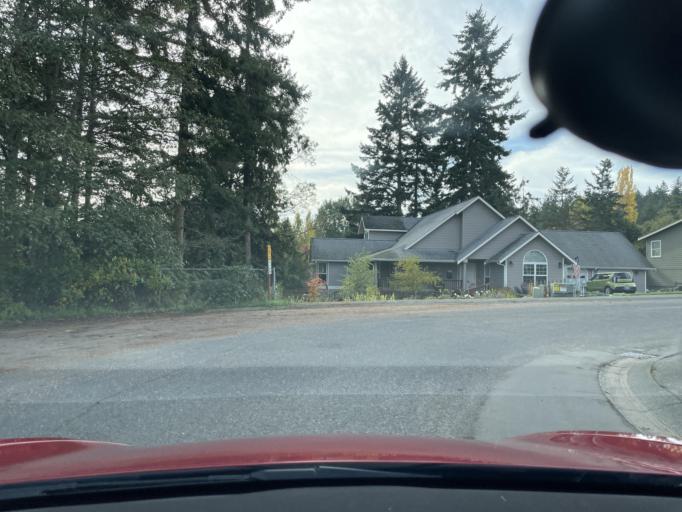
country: US
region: Washington
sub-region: San Juan County
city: Friday Harbor
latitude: 48.5405
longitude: -123.0302
